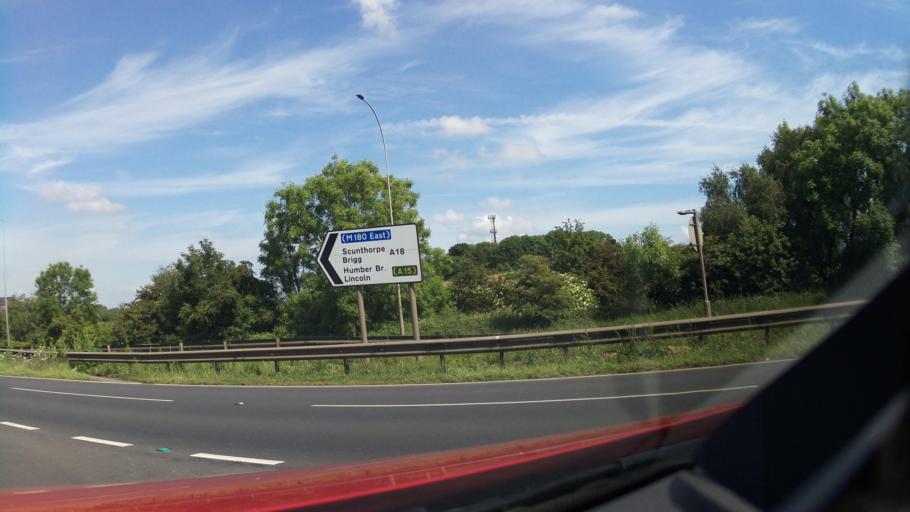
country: GB
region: England
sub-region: North Lincolnshire
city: Broughton
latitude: 53.5553
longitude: -0.5854
